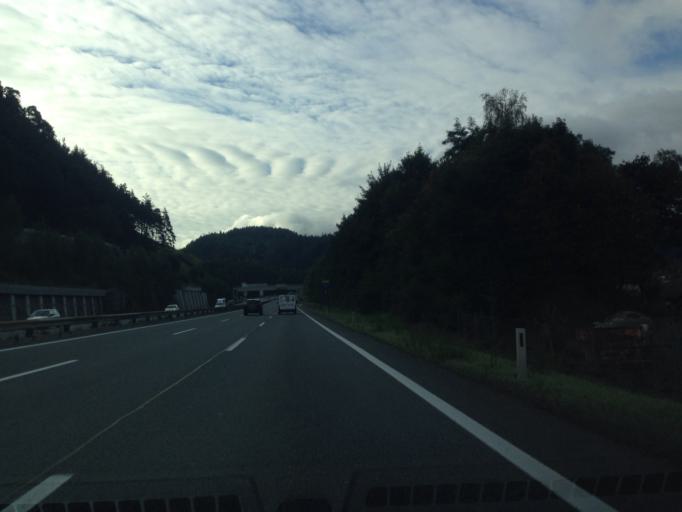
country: AT
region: Tyrol
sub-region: Politischer Bezirk Innsbruck Land
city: Mutters
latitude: 47.2335
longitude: 11.3923
